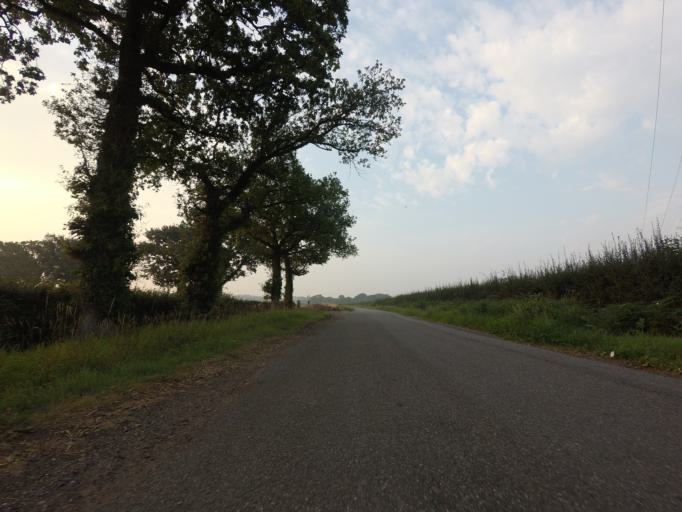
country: GB
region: England
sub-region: Kent
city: Lenham
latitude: 51.1744
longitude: 0.7308
